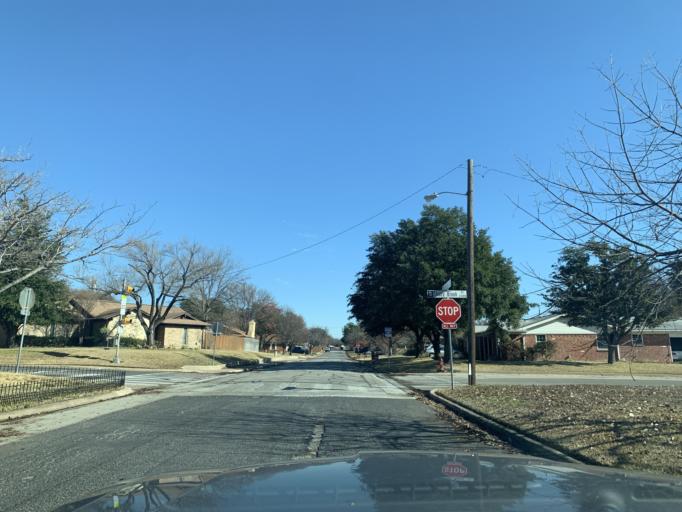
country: US
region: Texas
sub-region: Tarrant County
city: Bedford
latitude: 32.8492
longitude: -97.1532
